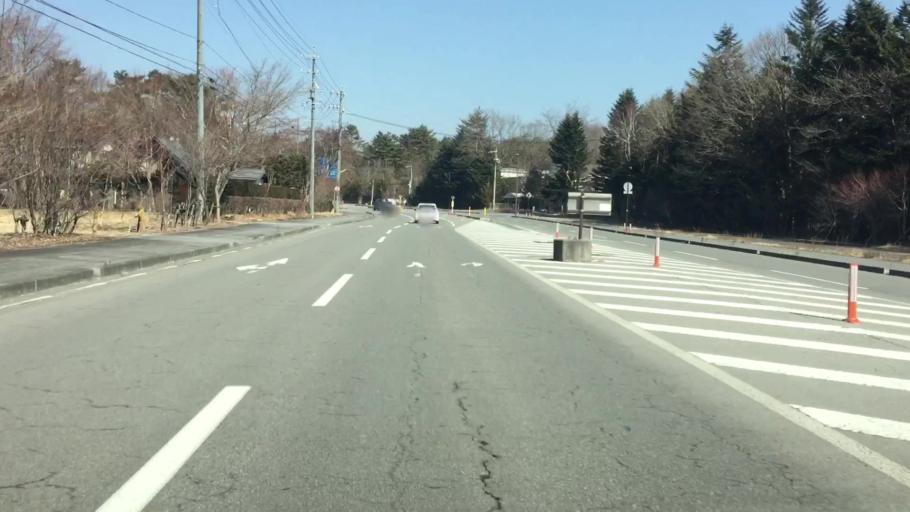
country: JP
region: Nagano
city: Saku
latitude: 36.3186
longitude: 138.6309
